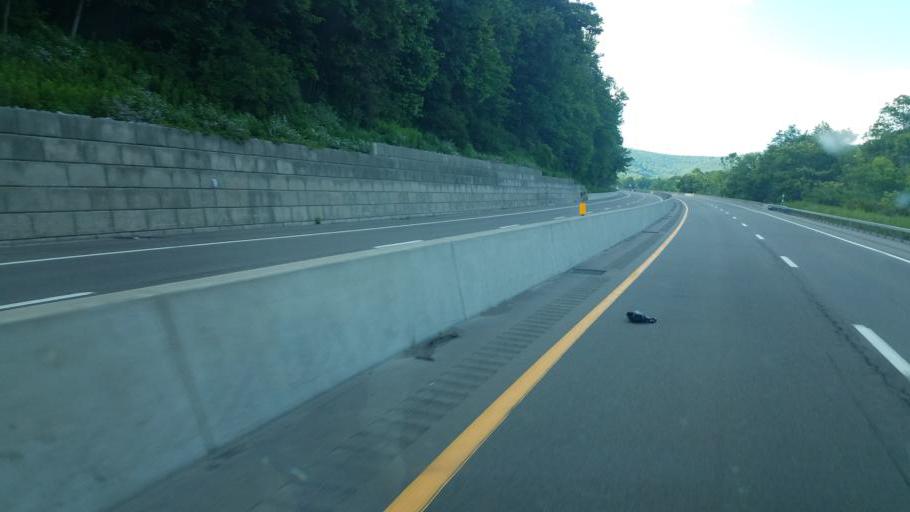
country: US
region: New York
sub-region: Cattaraugus County
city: Salamanca
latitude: 42.1351
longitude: -78.6654
